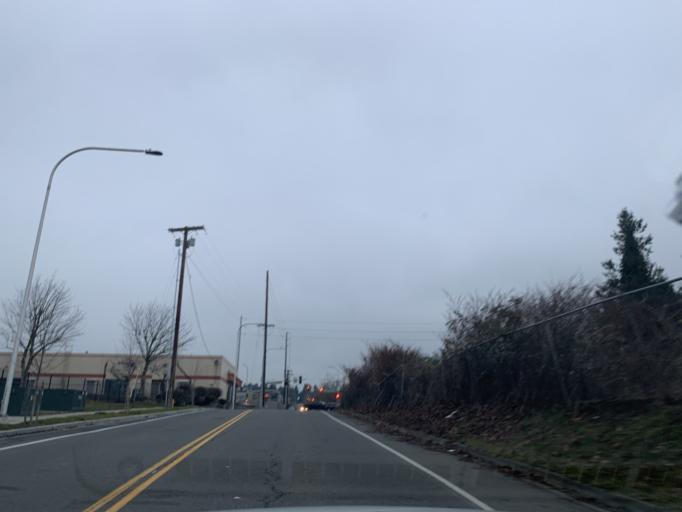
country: US
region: Washington
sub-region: King County
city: Federal Way
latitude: 47.2935
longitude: -122.3175
